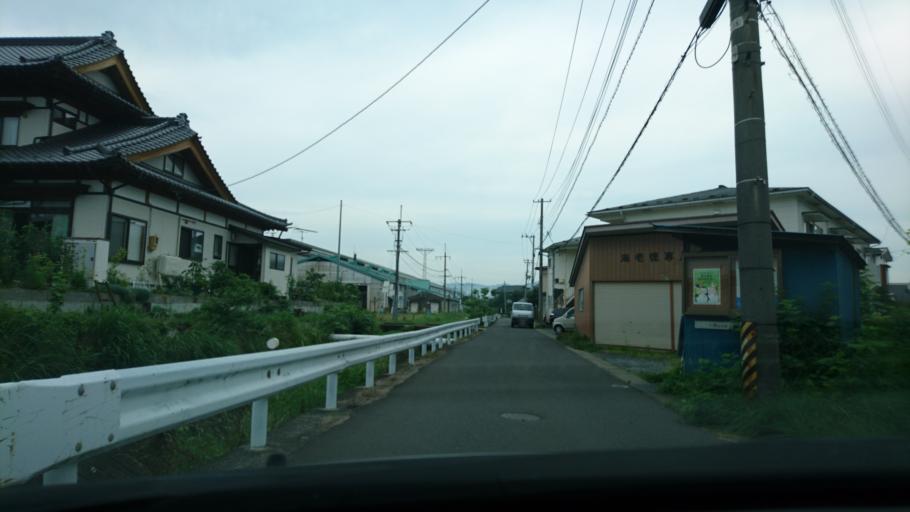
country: JP
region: Iwate
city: Ichinoseki
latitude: 38.9232
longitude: 141.1387
